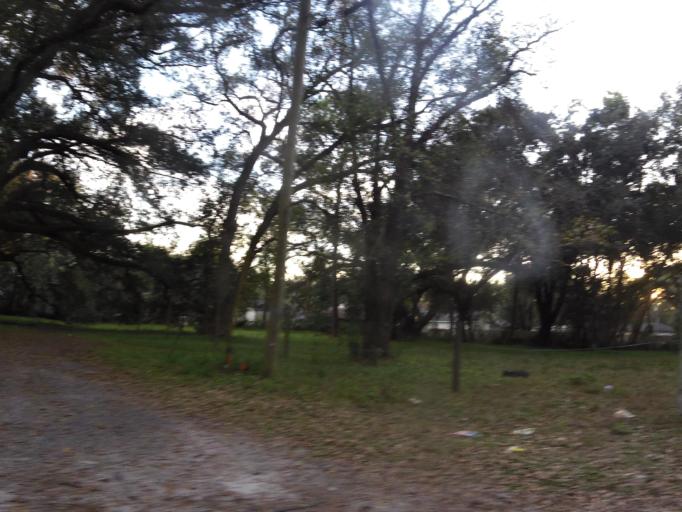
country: US
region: Florida
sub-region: Duval County
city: Jacksonville
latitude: 30.2818
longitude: -81.6395
